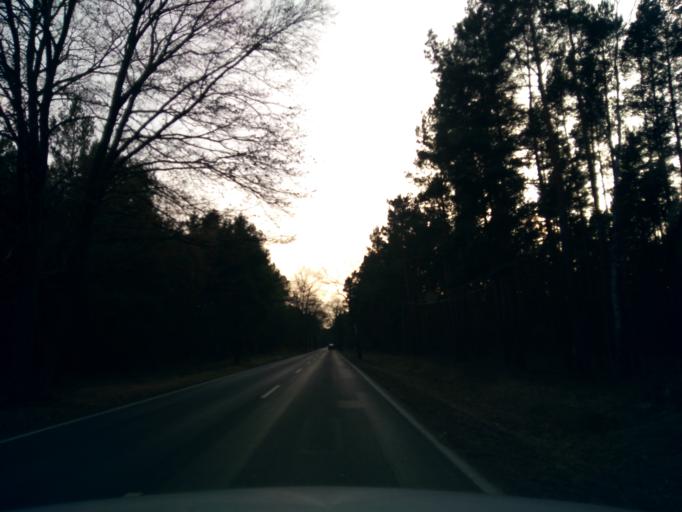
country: DE
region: Brandenburg
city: Glienicke
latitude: 52.7034
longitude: 13.3658
